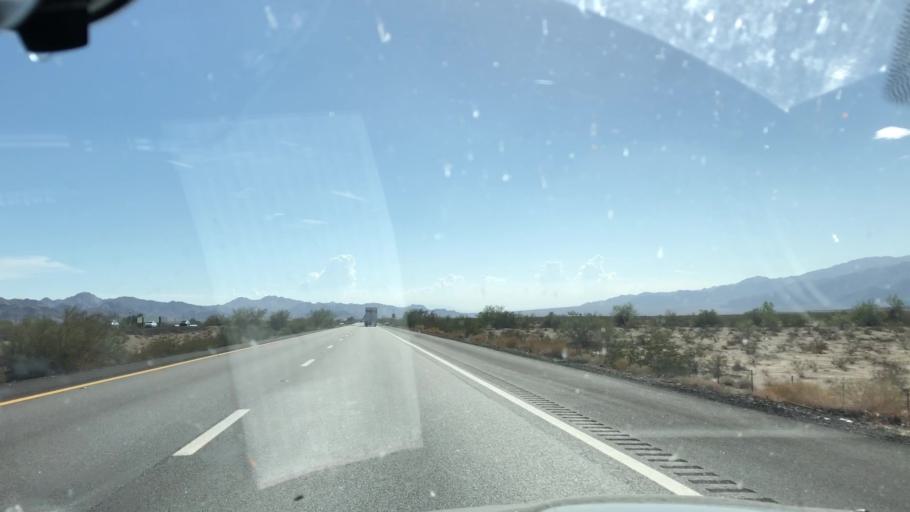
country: US
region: California
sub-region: Imperial County
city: Niland
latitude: 33.6817
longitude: -115.5464
